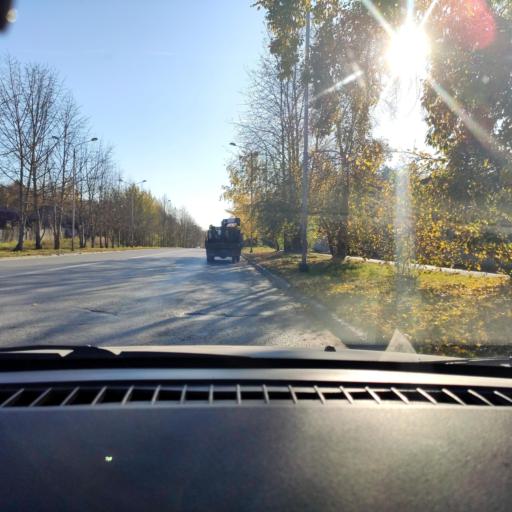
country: RU
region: Perm
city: Perm
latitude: 58.0797
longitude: 56.3728
